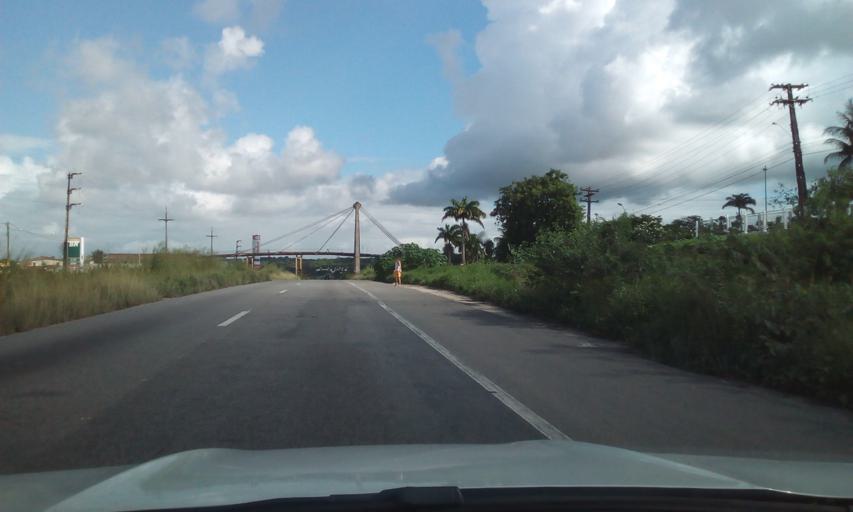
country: BR
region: Pernambuco
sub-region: Abreu E Lima
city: Abreu e Lima
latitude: -7.9361
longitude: -34.9032
